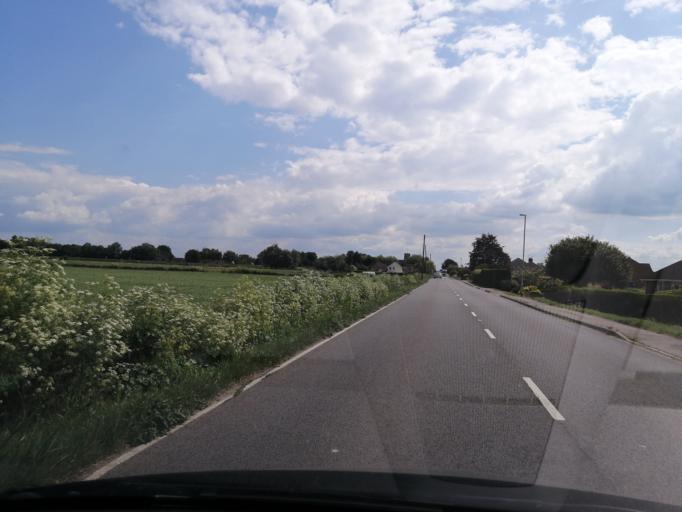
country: GB
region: England
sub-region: Cambridgeshire
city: Ramsey
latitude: 52.4731
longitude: -0.1528
